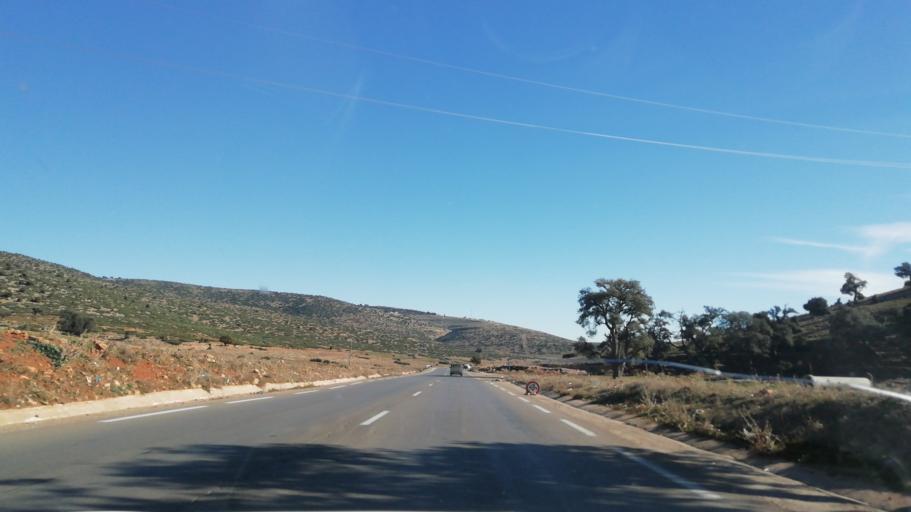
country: DZ
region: Tlemcen
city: Sebdou
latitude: 34.7150
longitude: -1.3282
